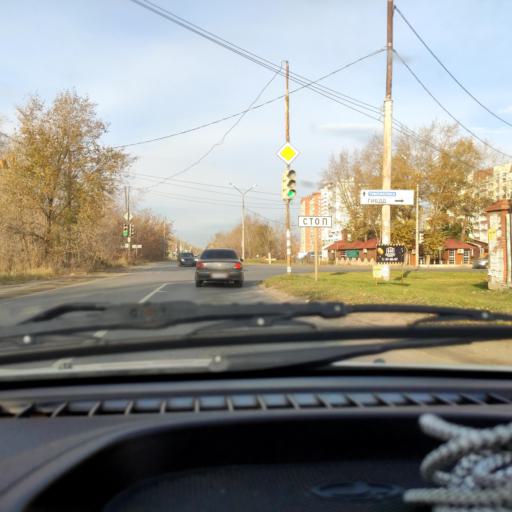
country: RU
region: Samara
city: Tol'yatti
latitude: 53.5378
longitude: 49.3932
